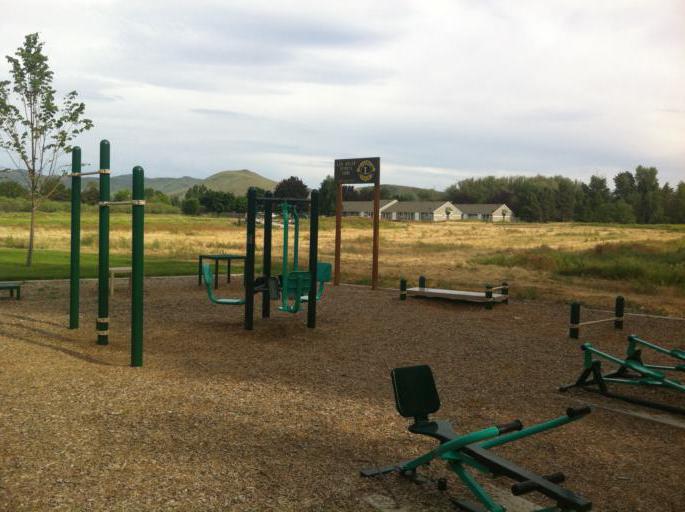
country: US
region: Oregon
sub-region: Baker County
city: Baker City
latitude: 44.7889
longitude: -117.8307
